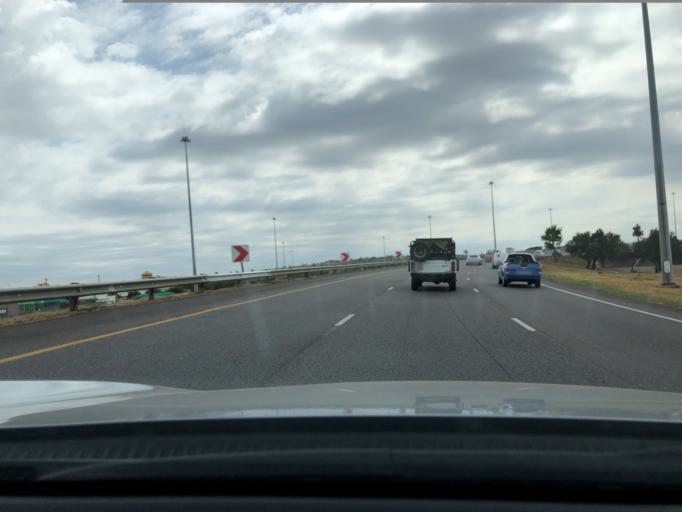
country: ZA
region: Gauteng
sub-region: City of Tshwane Metropolitan Municipality
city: Centurion
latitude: -25.8771
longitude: 28.1671
